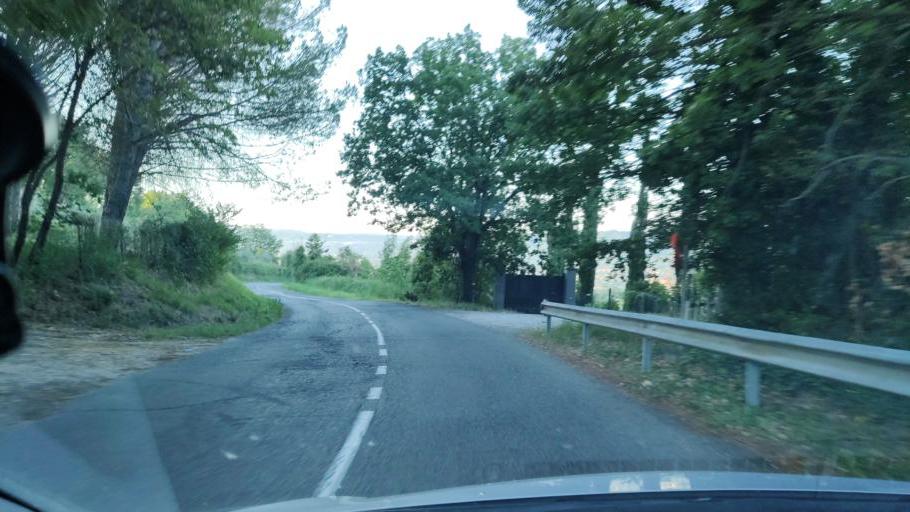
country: IT
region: Umbria
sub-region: Provincia di Terni
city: Giove
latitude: 42.5039
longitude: 12.3208
